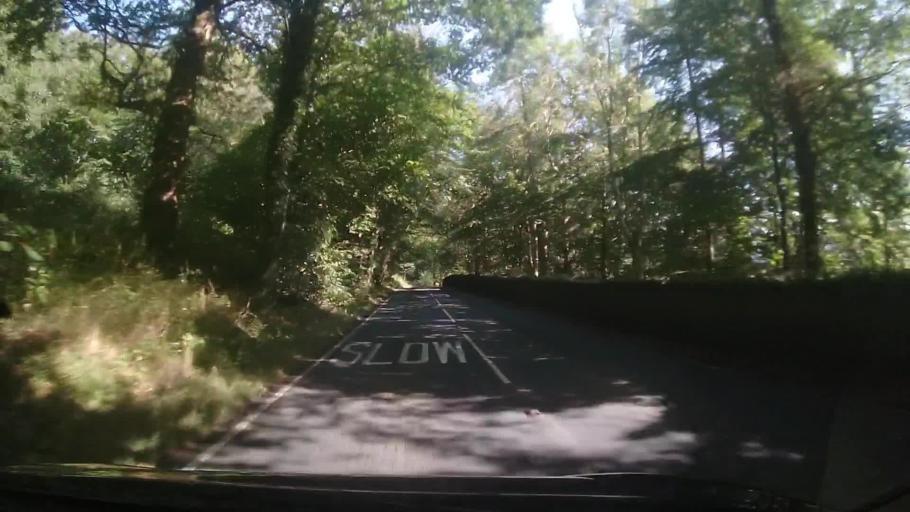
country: GB
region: England
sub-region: Cumbria
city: Seascale
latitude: 54.3586
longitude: -3.3791
